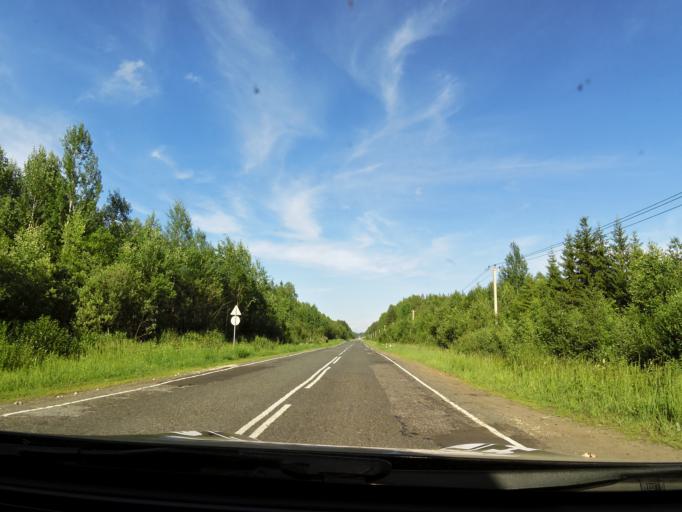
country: RU
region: Kirov
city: Belaya Kholunitsa
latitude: 58.9059
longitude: 51.0372
